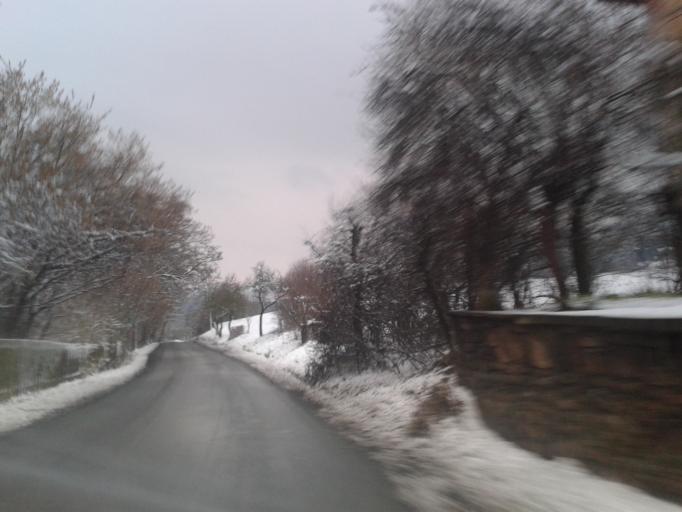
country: CZ
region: Central Bohemia
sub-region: Okres Beroun
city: Beroun
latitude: 49.9297
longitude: 14.0647
